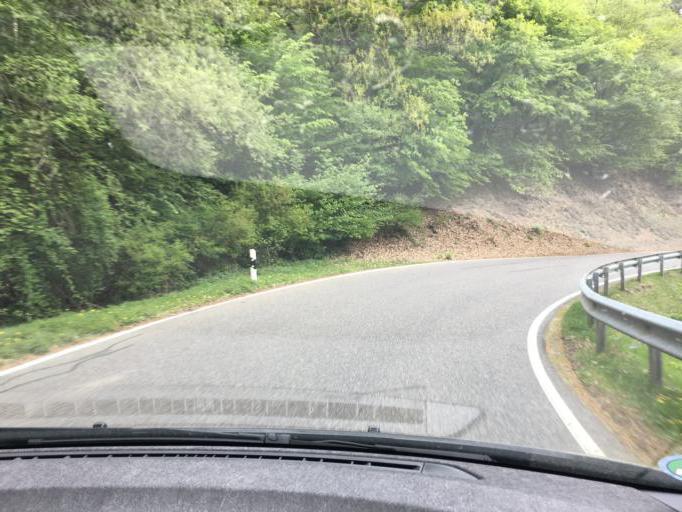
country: DE
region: Rheinland-Pfalz
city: Ahrbruck
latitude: 50.4881
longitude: 6.9620
